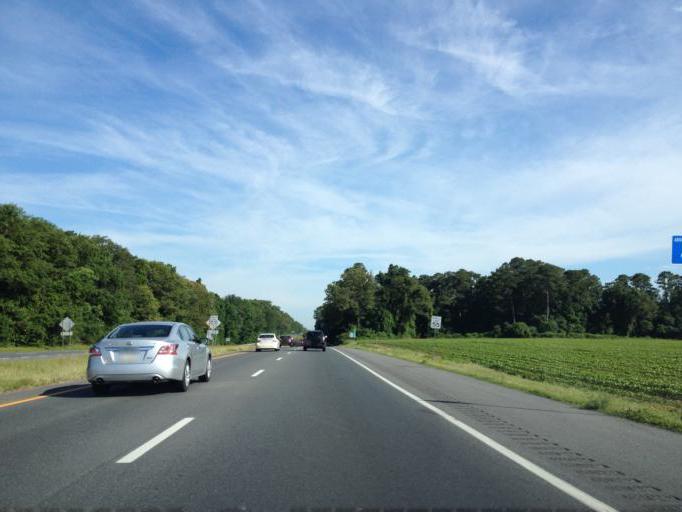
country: US
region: Delaware
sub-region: Sussex County
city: Millsboro
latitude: 38.6011
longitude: -75.3191
